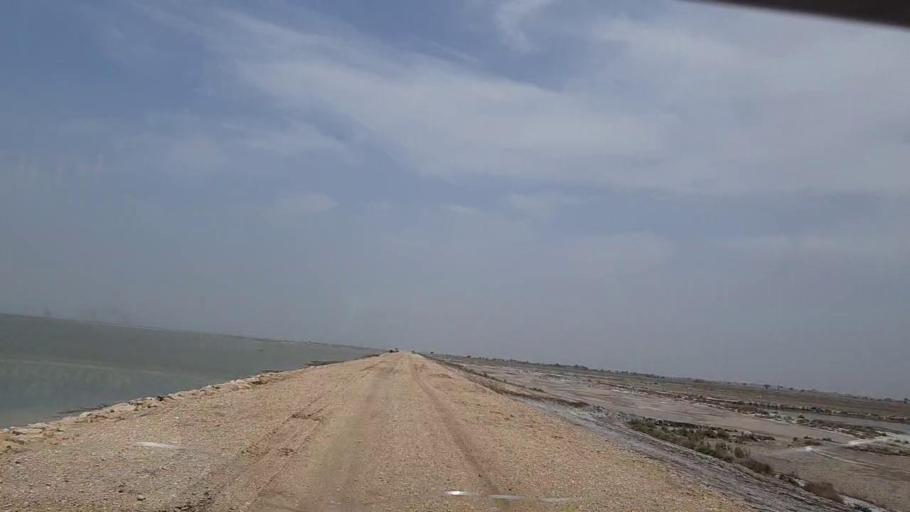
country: PK
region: Sindh
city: Sehwan
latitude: 26.4141
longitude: 67.7699
